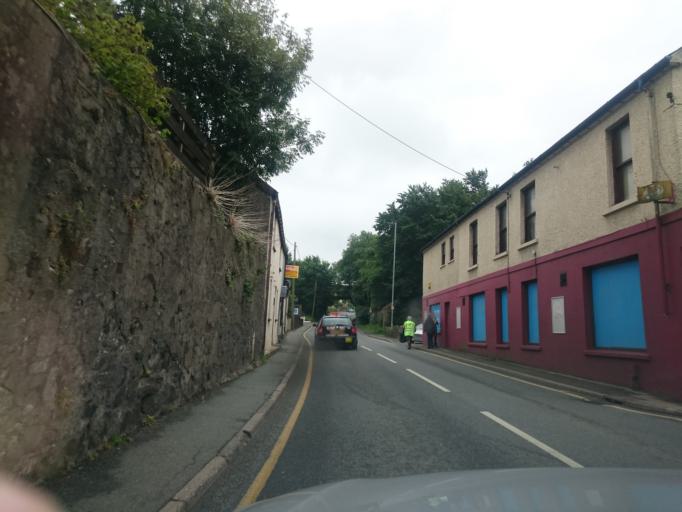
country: GB
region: Wales
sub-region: Pembrokeshire
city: Haverfordwest
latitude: 51.7914
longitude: -4.9775
